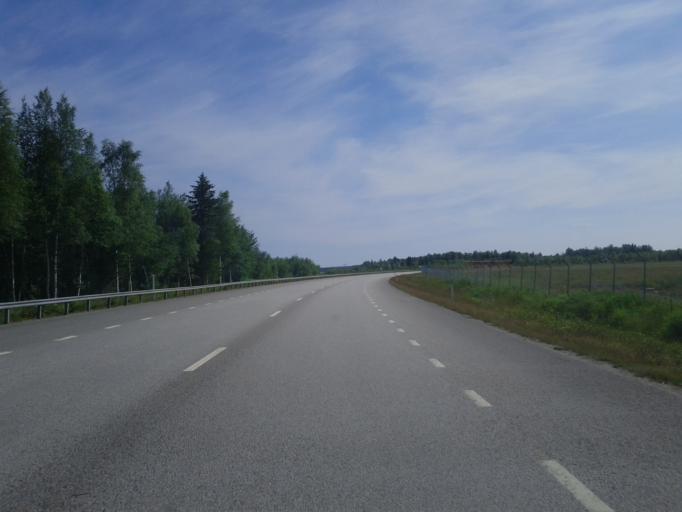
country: SE
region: Vaesterbotten
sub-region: Umea Kommun
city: Umea
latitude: 63.7845
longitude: 20.3038
